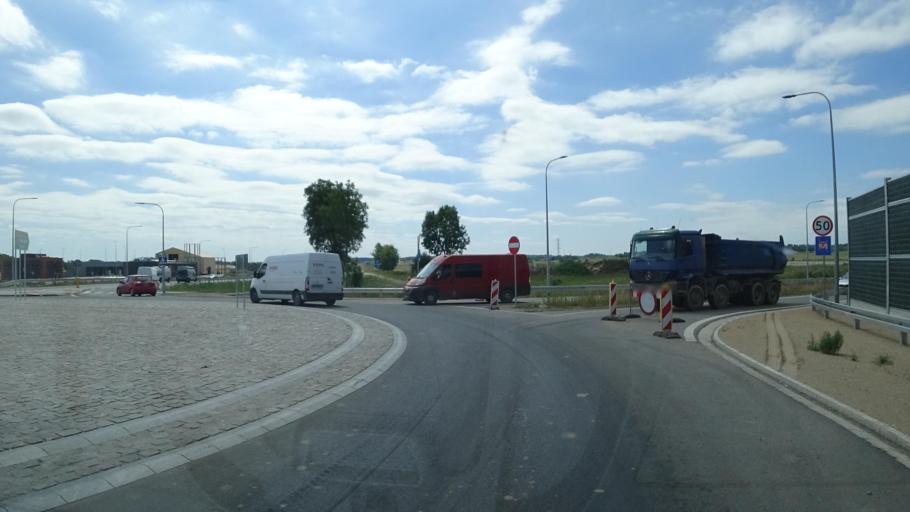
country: PL
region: Warmian-Masurian Voivodeship
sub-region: Powiat elcki
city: Elk
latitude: 53.7591
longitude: 22.3384
